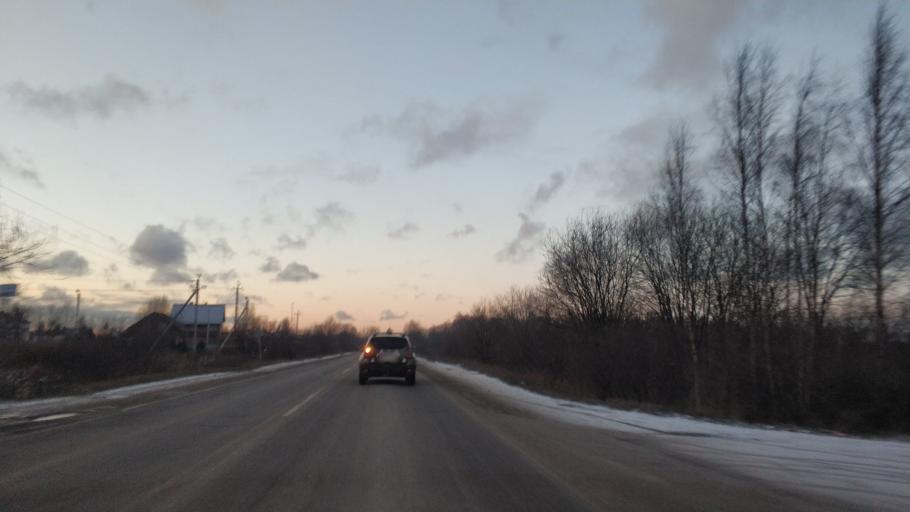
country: RU
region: St.-Petersburg
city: Pontonnyy
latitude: 59.8041
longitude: 30.6276
